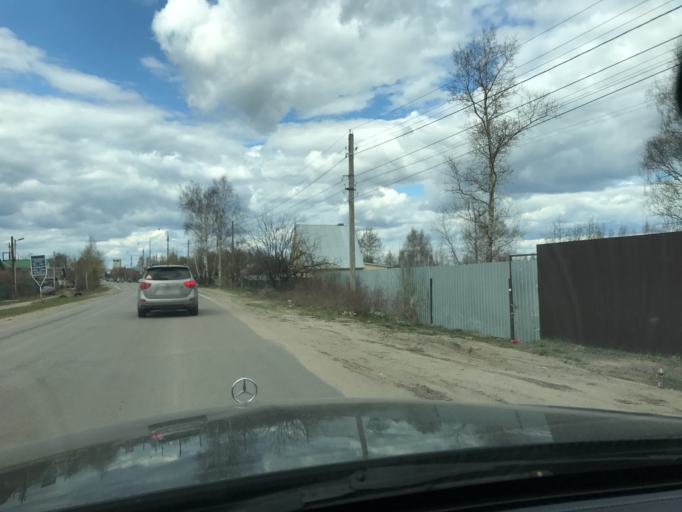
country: RU
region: Vladimir
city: Pokrov
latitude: 55.8923
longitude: 39.2136
